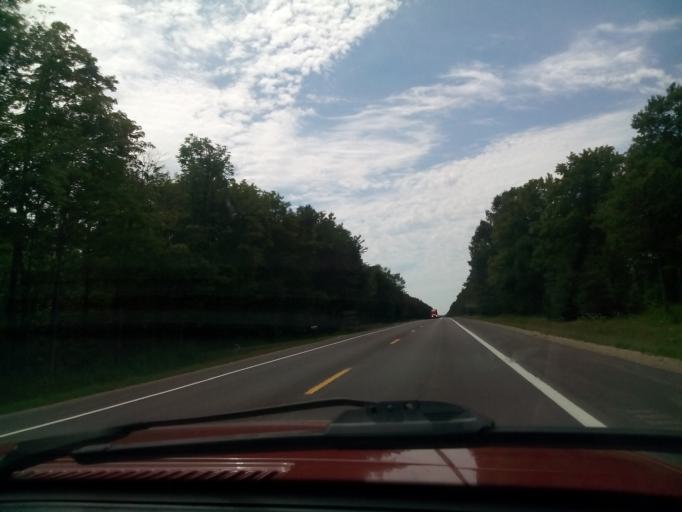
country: US
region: Michigan
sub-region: Schoolcraft County
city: Manistique
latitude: 46.0552
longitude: -85.9618
